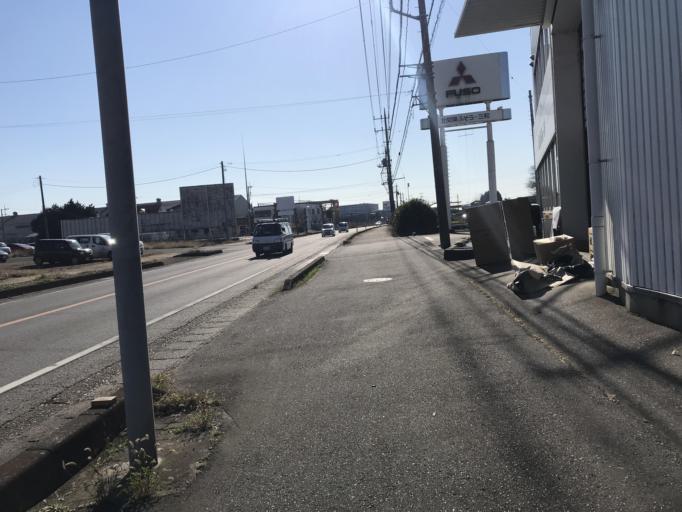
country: JP
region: Ibaraki
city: Sakai
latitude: 36.1424
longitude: 139.8108
